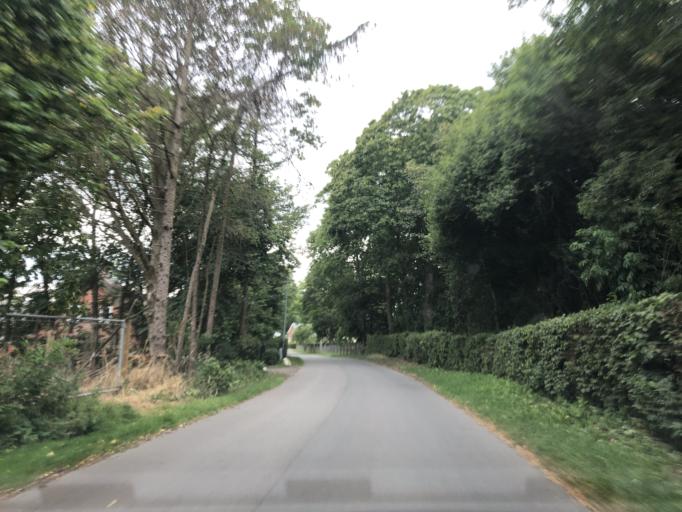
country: DK
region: Central Jutland
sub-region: Skanderborg Kommune
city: Ry
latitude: 56.1499
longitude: 9.7866
